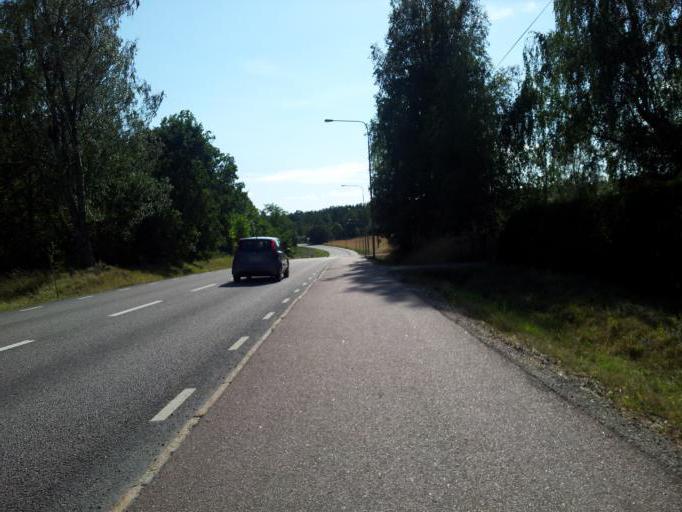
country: SE
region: Uppsala
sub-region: Knivsta Kommun
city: Knivsta
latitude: 59.8709
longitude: 17.9528
